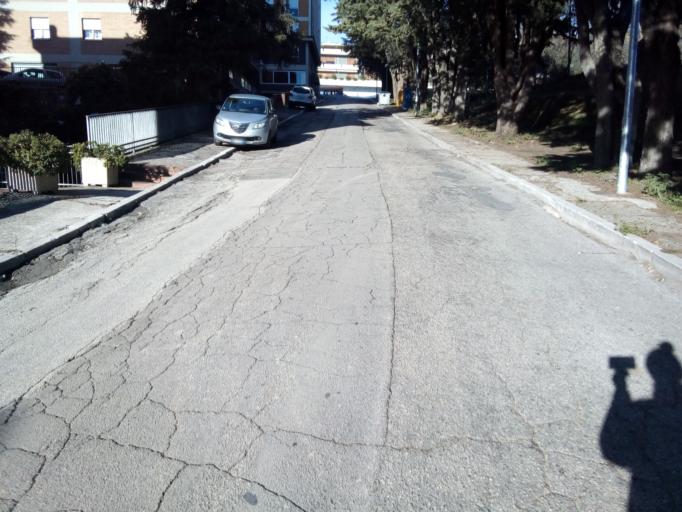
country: IT
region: Umbria
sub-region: Provincia di Perugia
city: Perugia
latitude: 43.0948
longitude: 12.3927
